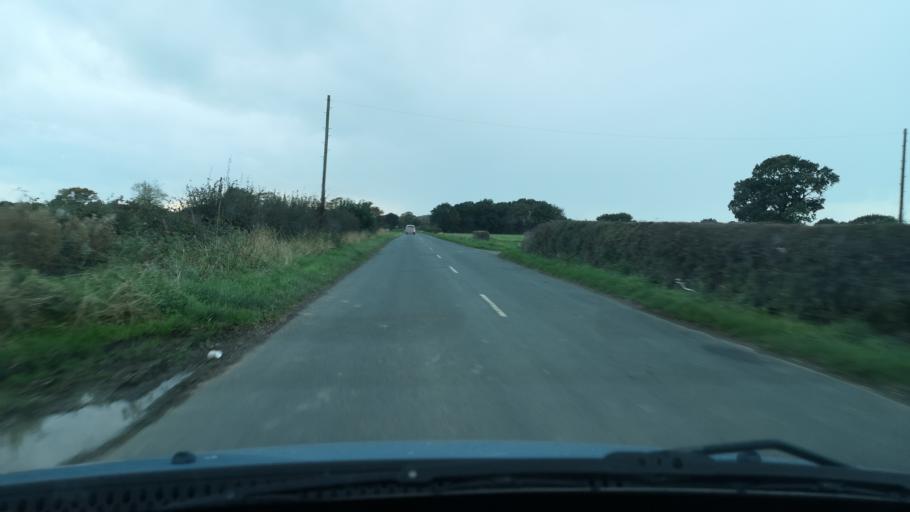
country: GB
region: England
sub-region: Doncaster
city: Stainforth
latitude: 53.6169
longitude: -1.0405
